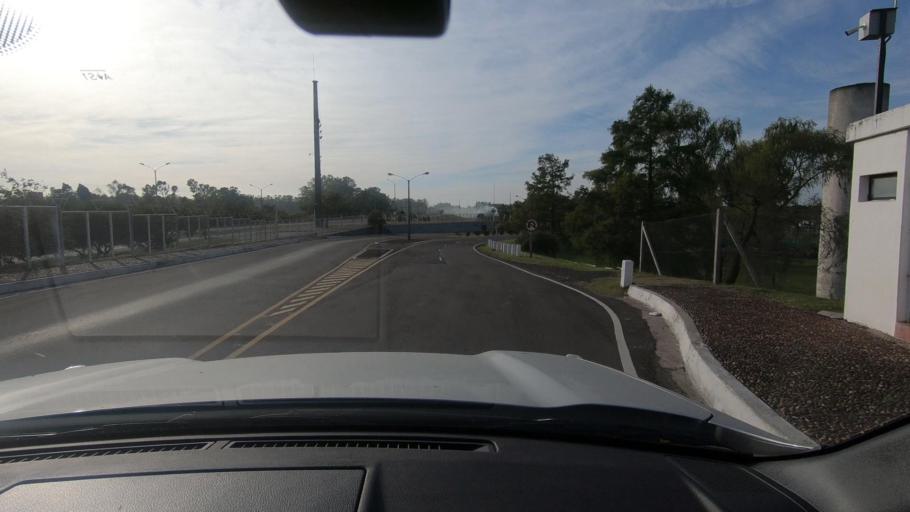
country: AR
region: Entre Rios
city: Colon
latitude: -32.2459
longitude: -58.1481
